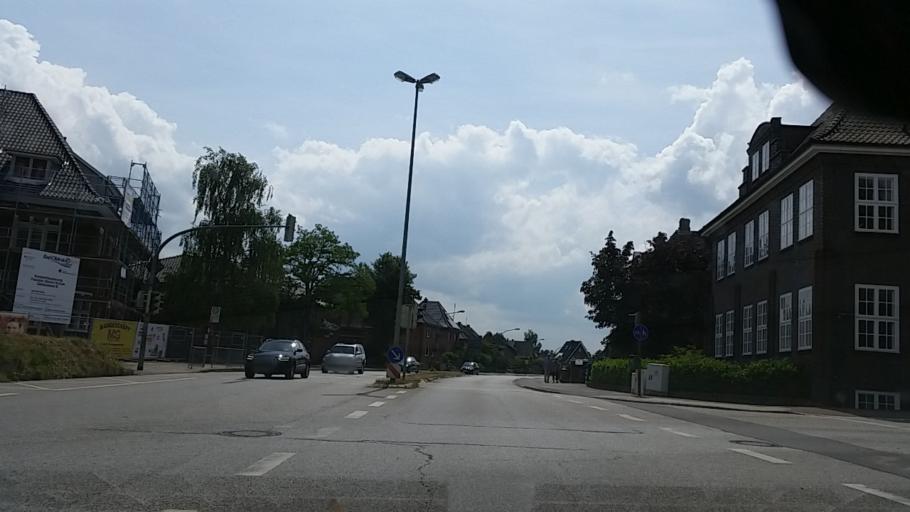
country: DE
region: Schleswig-Holstein
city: Bad Oldesloe
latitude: 53.8074
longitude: 10.3644
